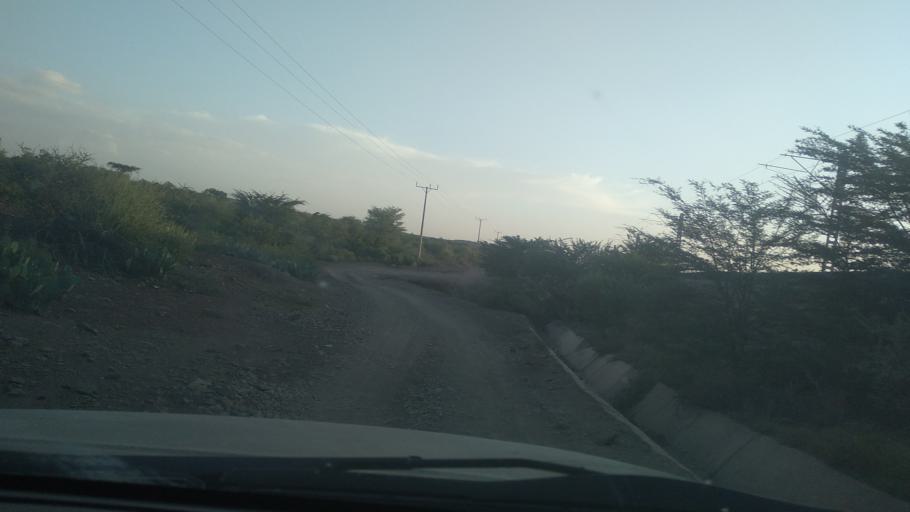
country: ET
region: Oromiya
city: Asbe Teferi
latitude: 9.2615
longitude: 40.7973
